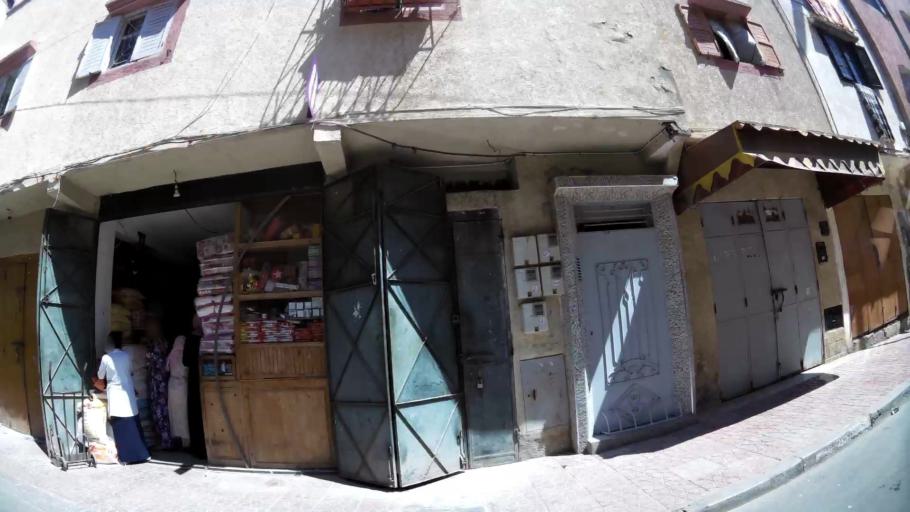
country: MA
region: Rabat-Sale-Zemmour-Zaer
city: Sale
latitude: 34.0650
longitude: -6.7778
